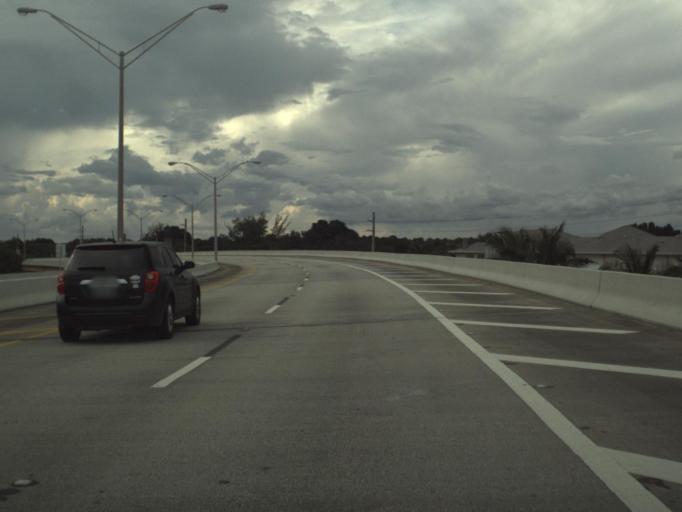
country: US
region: Florida
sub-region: Miami-Dade County
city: South Miami
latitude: 25.6951
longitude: -80.3063
